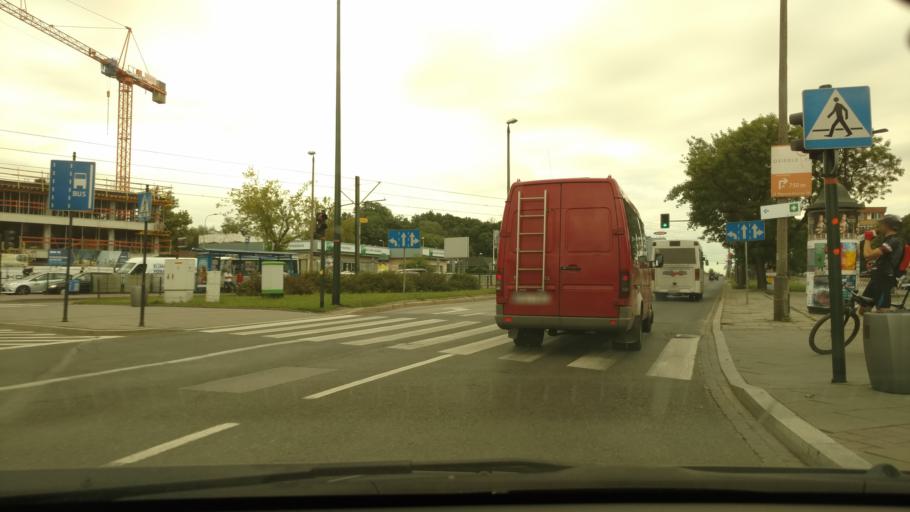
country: PL
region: Lesser Poland Voivodeship
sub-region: Krakow
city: Krakow
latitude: 50.0364
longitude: 19.9402
